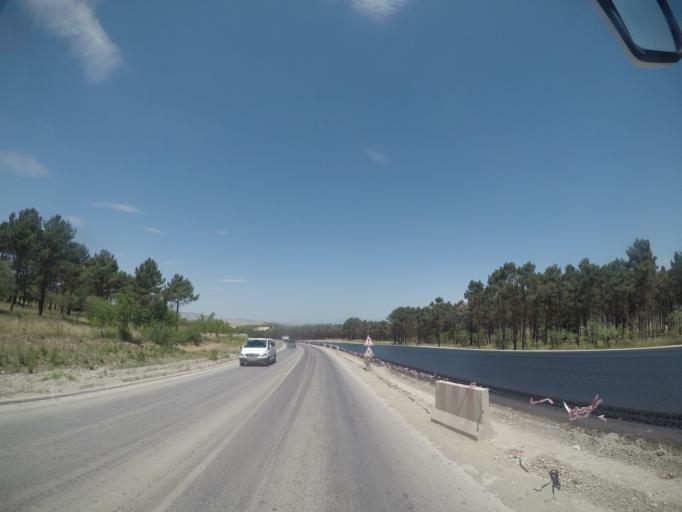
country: AZ
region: Qobustan
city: Qobustan
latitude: 40.5269
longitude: 48.7992
